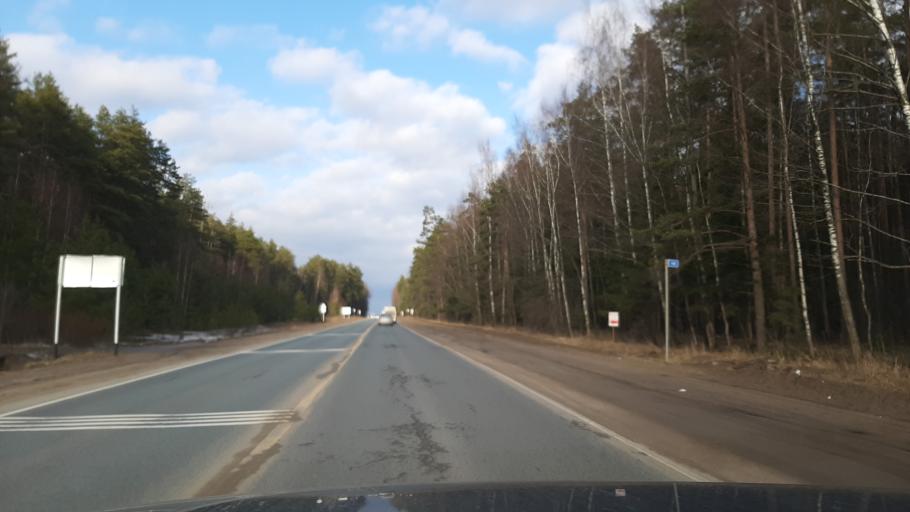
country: RU
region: Ivanovo
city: Teykovo
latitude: 56.8778
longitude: 40.5921
